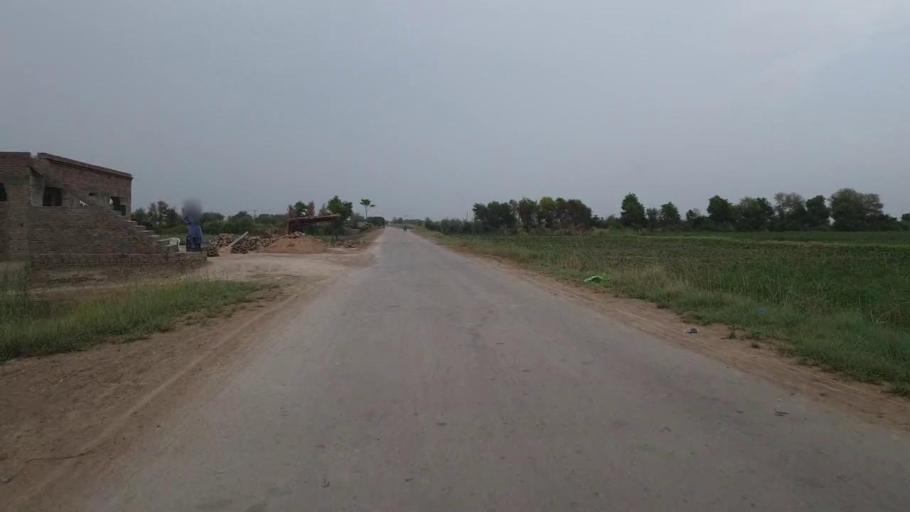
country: PK
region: Sindh
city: Bandhi
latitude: 26.5346
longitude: 68.2194
